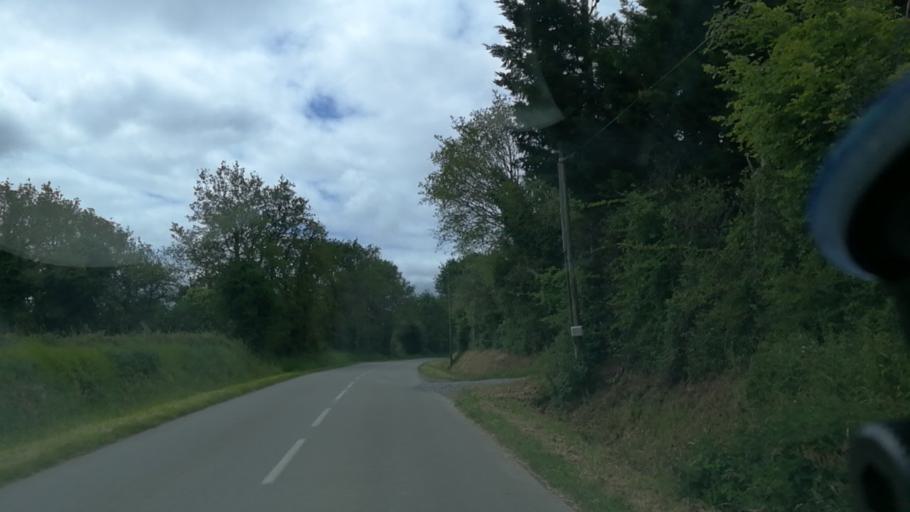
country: FR
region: Brittany
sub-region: Departement du Morbihan
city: Penestin
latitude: 47.4872
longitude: -2.4371
